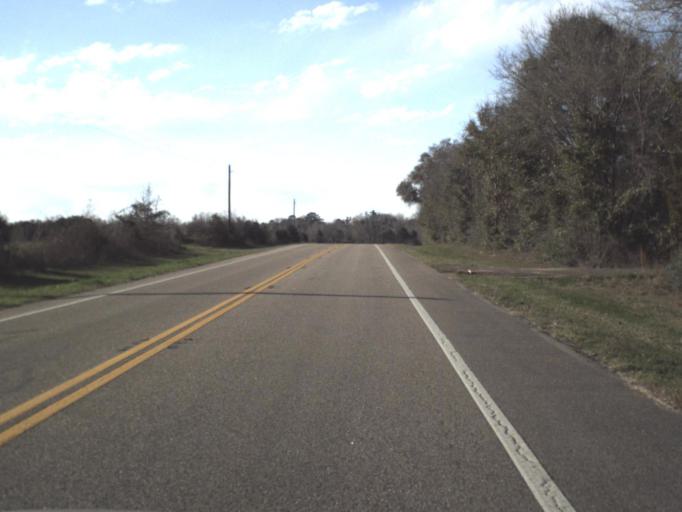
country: US
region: Florida
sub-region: Jackson County
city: Marianna
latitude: 30.6536
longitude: -85.2135
